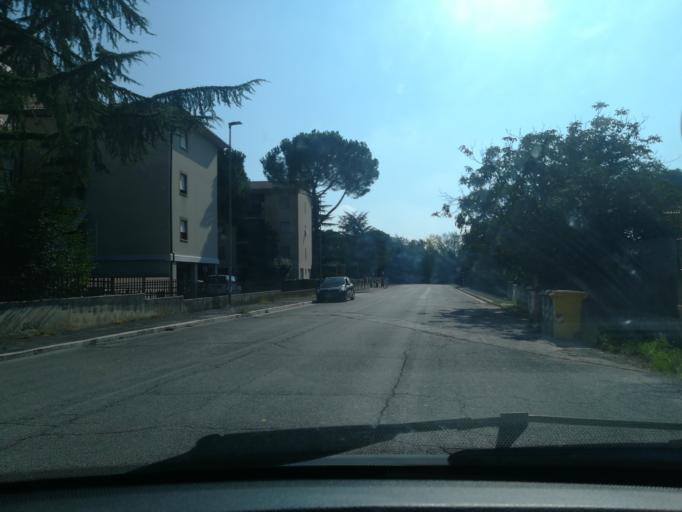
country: IT
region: The Marches
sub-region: Provincia di Macerata
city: Piediripa
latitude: 43.2745
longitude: 13.4767
